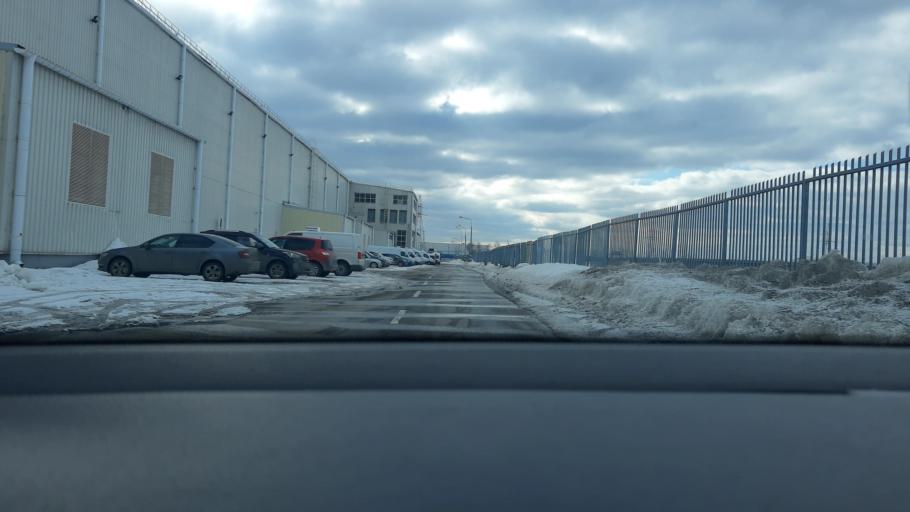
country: RU
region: Moskovskaya
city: Lesnyye Polyany
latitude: 55.9800
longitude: 37.8721
